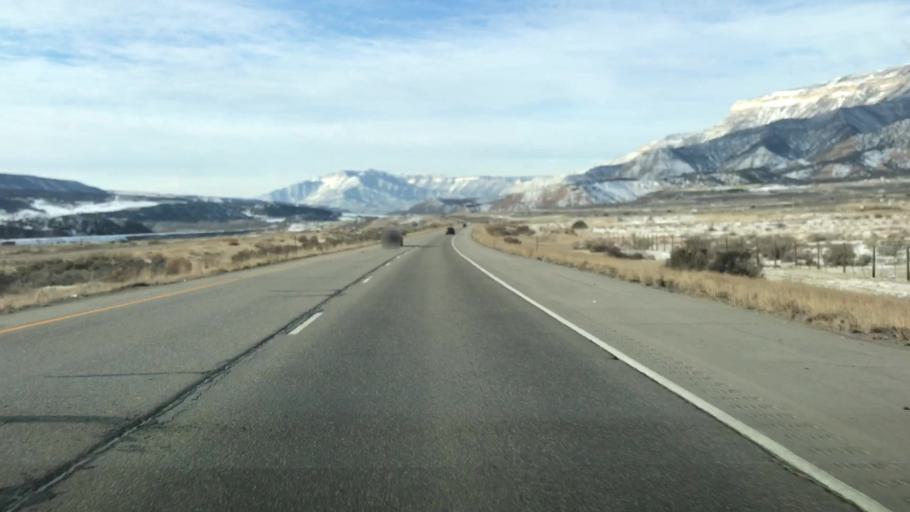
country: US
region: Colorado
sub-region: Garfield County
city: Rifle
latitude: 39.5065
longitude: -107.8874
